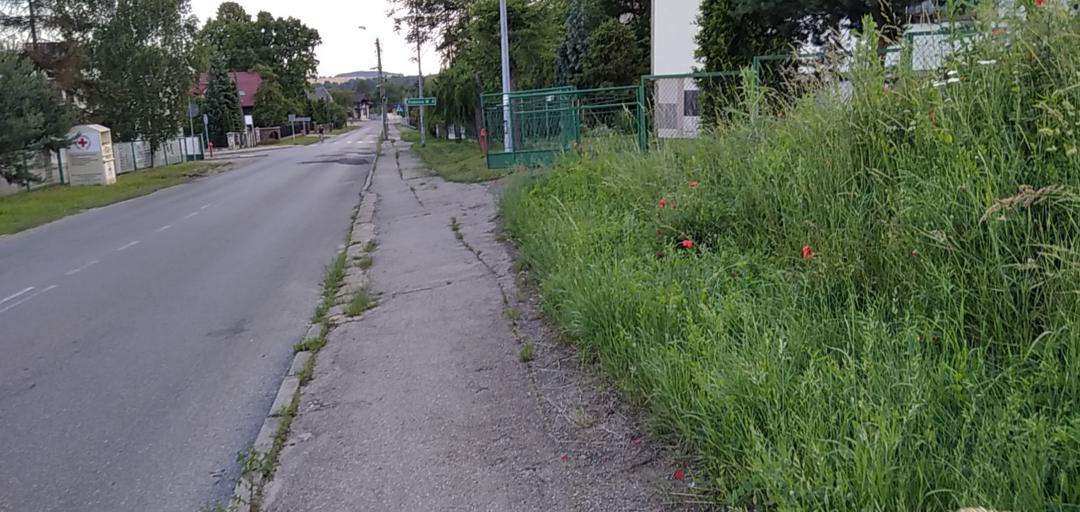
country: PL
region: Silesian Voivodeship
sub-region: Powiat bedzinski
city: Sarnow
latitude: 50.4076
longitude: 19.1392
